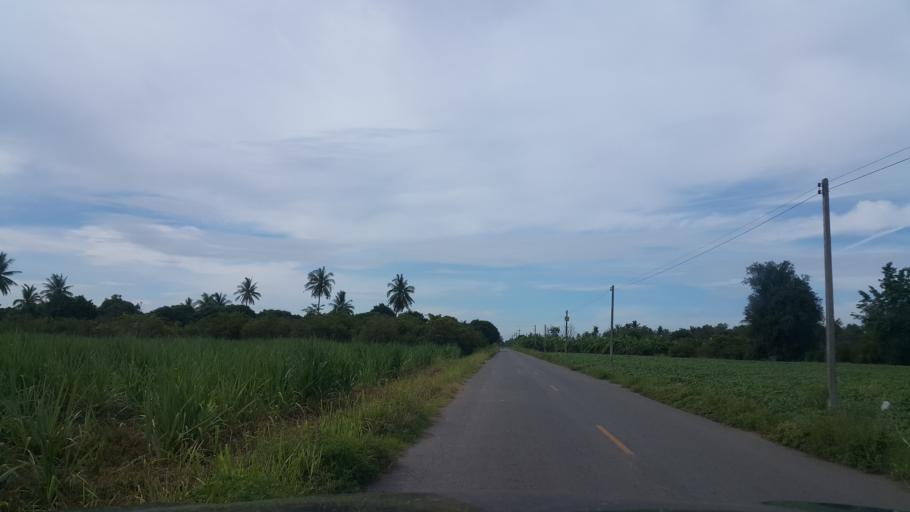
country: TH
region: Sukhothai
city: Sawankhalok
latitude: 17.2739
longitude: 99.9059
